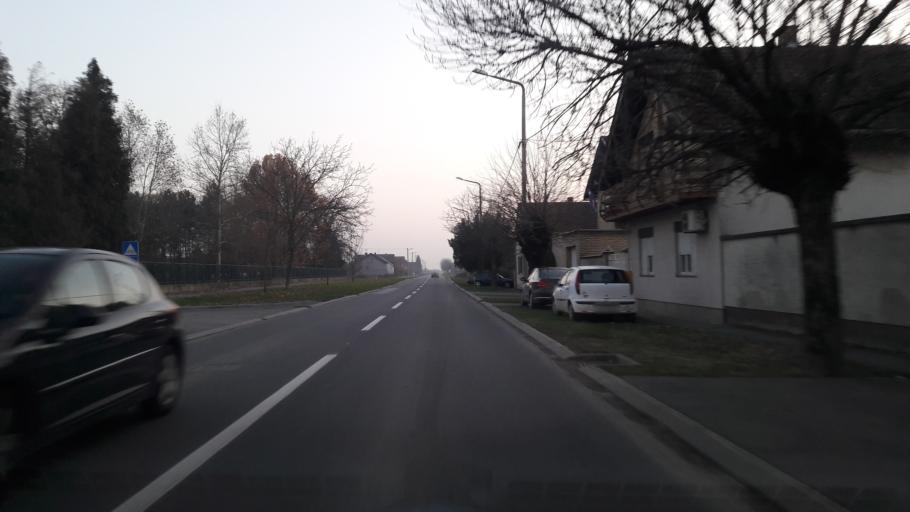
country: HR
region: Vukovarsko-Srijemska
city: Vukovar
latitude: 45.3310
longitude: 19.0025
